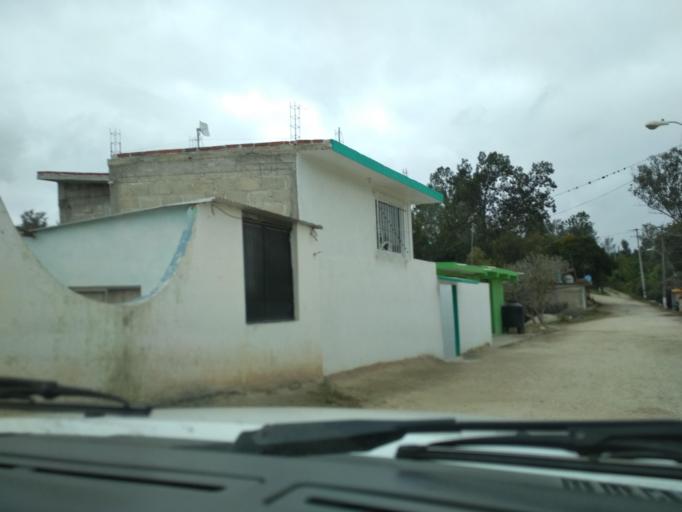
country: MX
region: Veracruz
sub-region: Emiliano Zapata
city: Dos Rios
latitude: 19.5380
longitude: -96.7975
